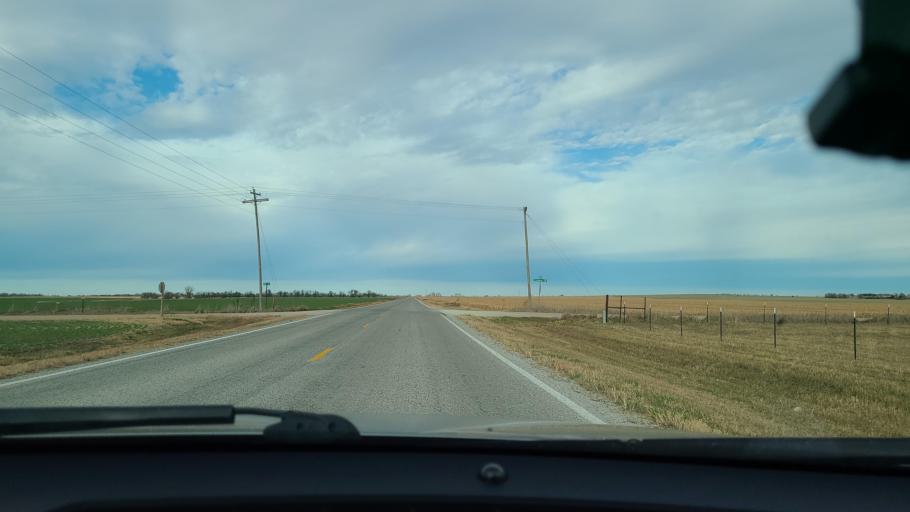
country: US
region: Kansas
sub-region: McPherson County
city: Inman
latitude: 38.3180
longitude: -97.9250
